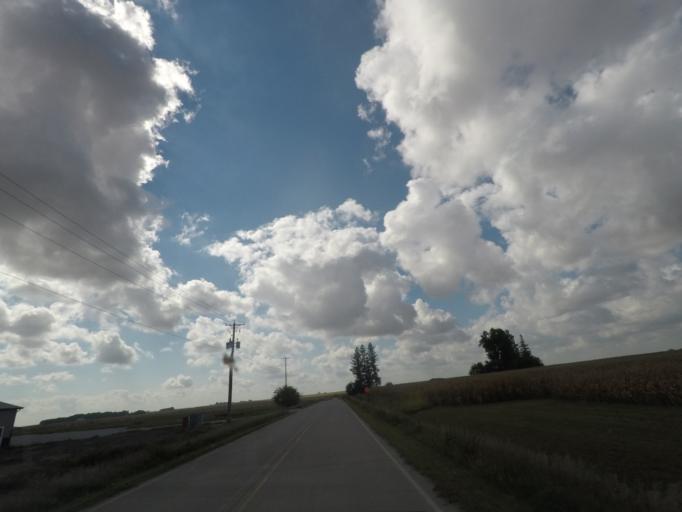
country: US
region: Iowa
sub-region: Story County
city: Nevada
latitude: 42.0057
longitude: -93.3192
